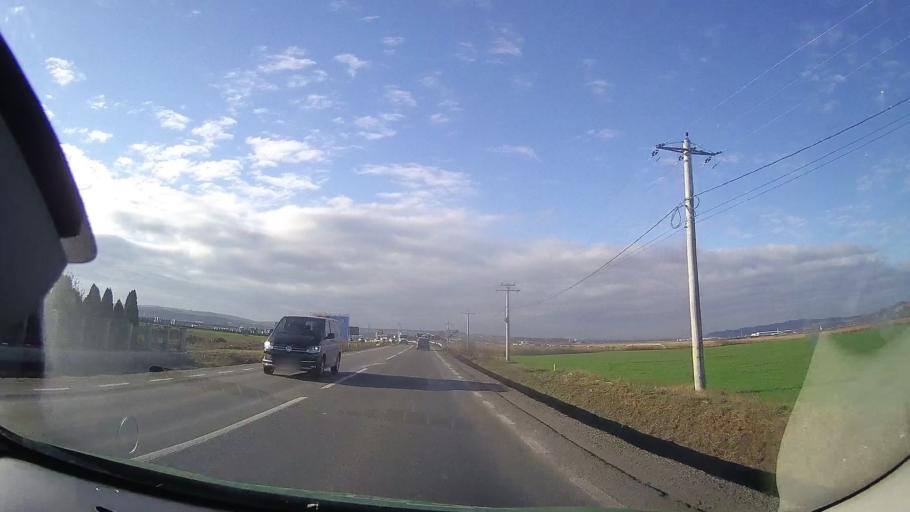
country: RO
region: Mures
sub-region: Comuna Ungheni
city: Ungheni
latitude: 46.4742
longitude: 24.4467
